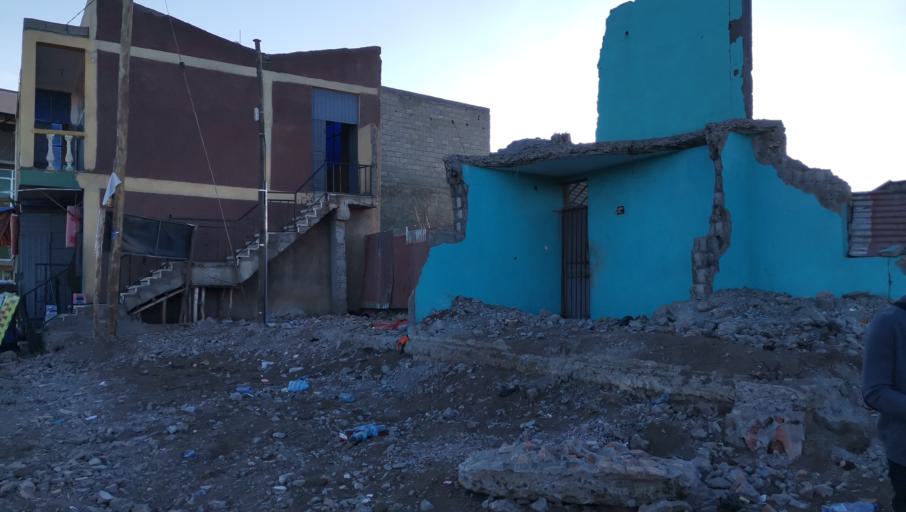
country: ET
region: Tigray
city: Korem
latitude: 12.6258
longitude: 39.0349
